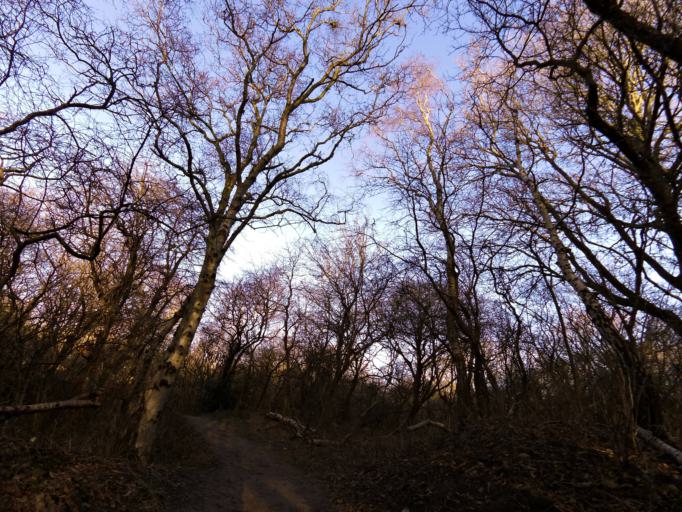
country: NL
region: South Holland
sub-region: Gemeente Hellevoetsluis
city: Nieuw-Helvoet
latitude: 51.9022
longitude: 4.0603
